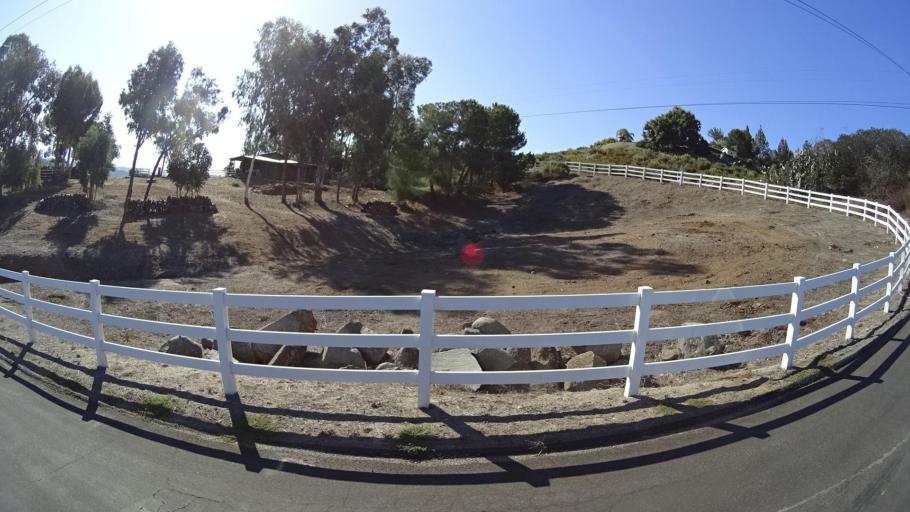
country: US
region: California
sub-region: San Diego County
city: Hidden Meadows
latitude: 33.2414
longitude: -117.1178
